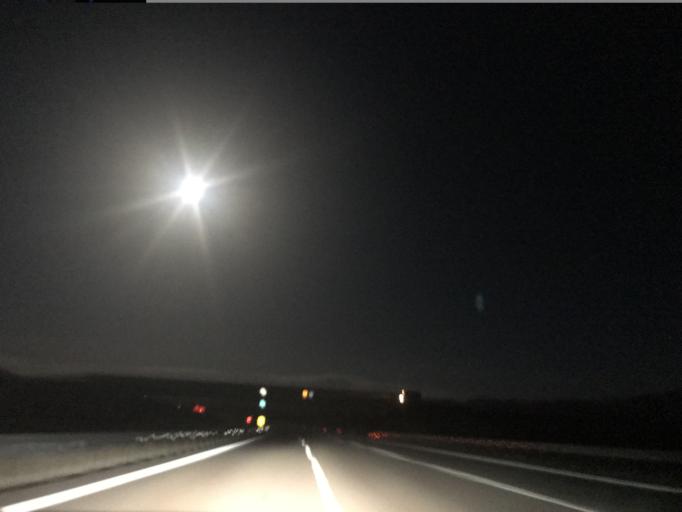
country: TR
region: Nigde
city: Ulukisla
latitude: 37.6309
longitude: 34.4581
